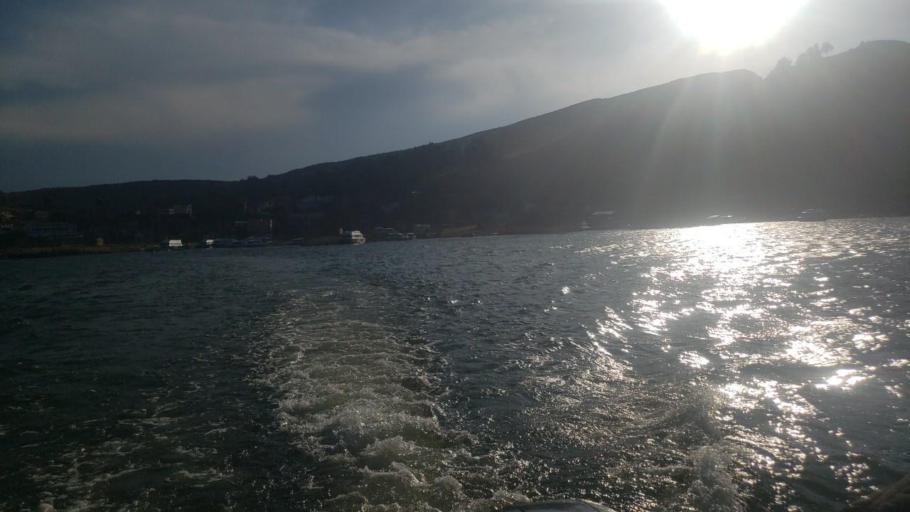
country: BO
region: La Paz
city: San Pedro
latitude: -16.3036
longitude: -68.7547
